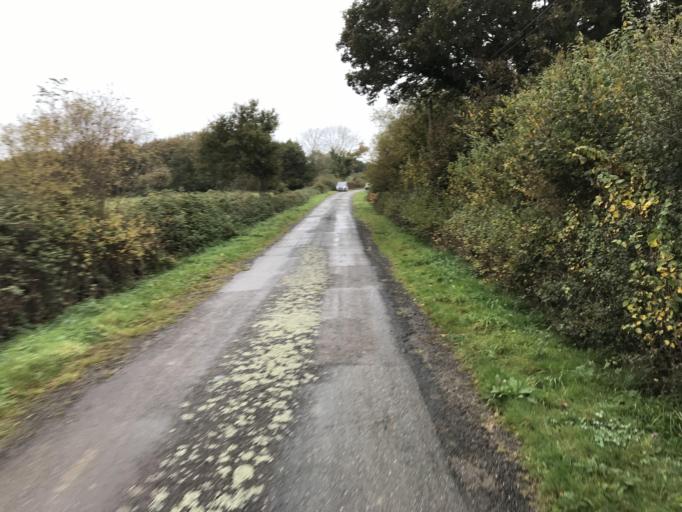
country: FR
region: Brittany
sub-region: Departement du Finistere
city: Logonna-Daoulas
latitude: 48.3375
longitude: -4.2766
